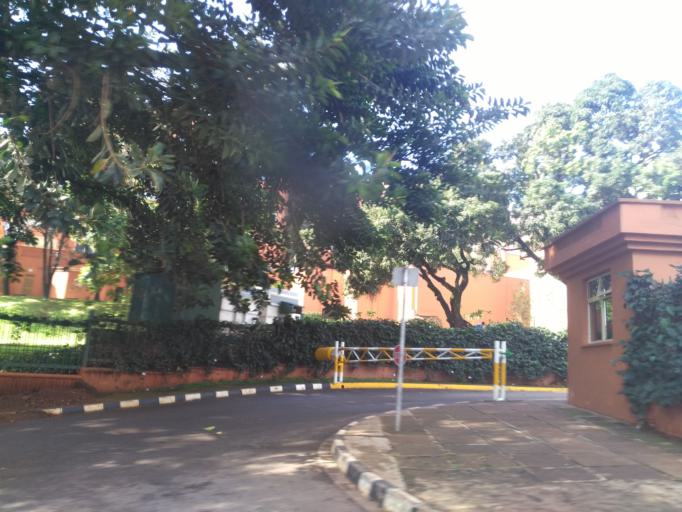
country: UG
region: Central Region
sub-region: Kampala District
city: Kampala
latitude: 0.3198
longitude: 32.5872
